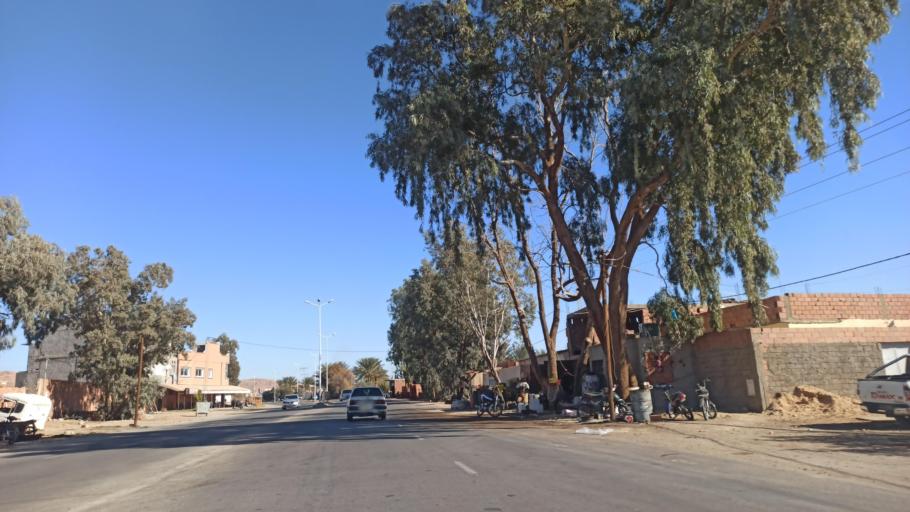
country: TN
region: Gafsa
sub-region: Gafsa Municipality
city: Gafsa
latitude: 34.4067
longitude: 8.7333
